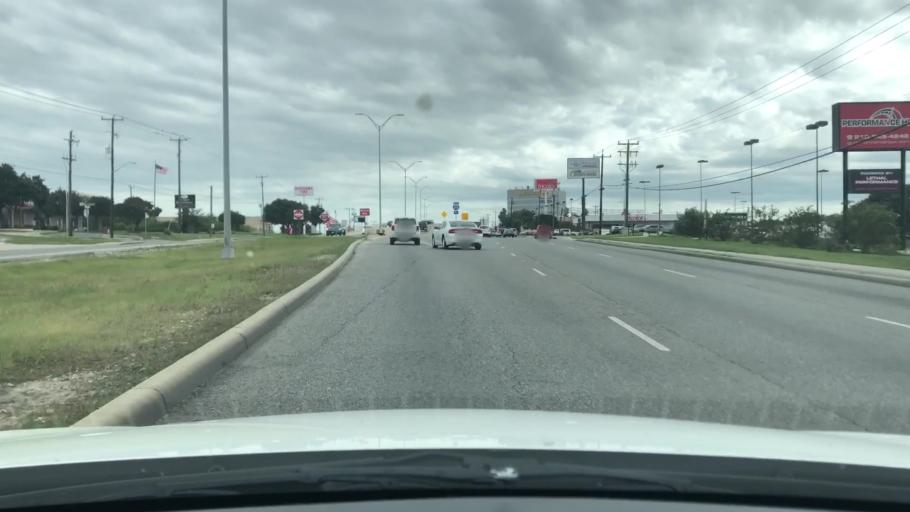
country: US
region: Texas
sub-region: Bexar County
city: Leon Valley
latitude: 29.4887
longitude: -98.6098
